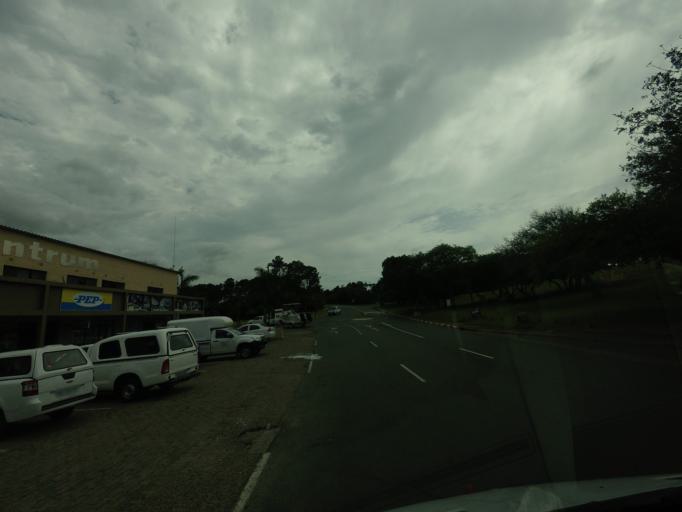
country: ZA
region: KwaZulu-Natal
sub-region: uMkhanyakude District Municipality
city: Mtubatuba
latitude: -28.3720
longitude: 32.4129
